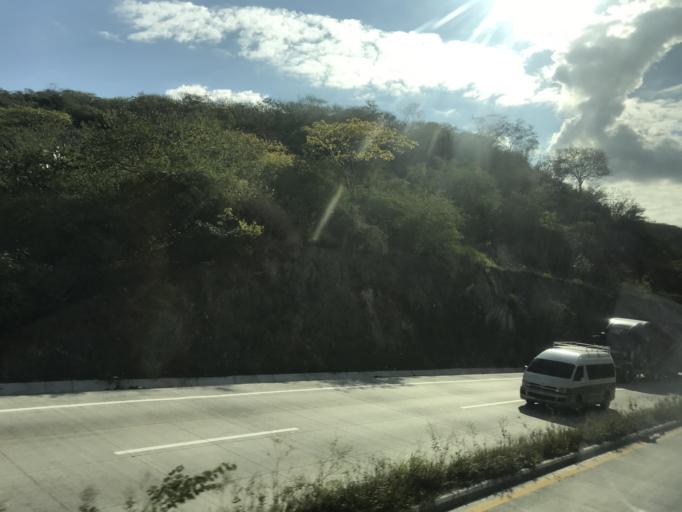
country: GT
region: El Progreso
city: Guastatoya
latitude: 14.8542
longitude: -90.0934
